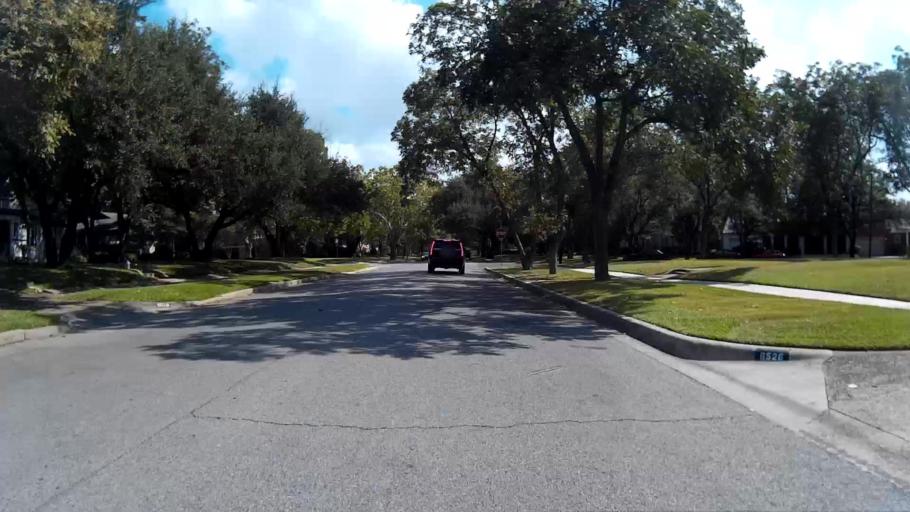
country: US
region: Texas
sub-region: Dallas County
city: Highland Park
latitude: 32.8182
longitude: -96.7505
